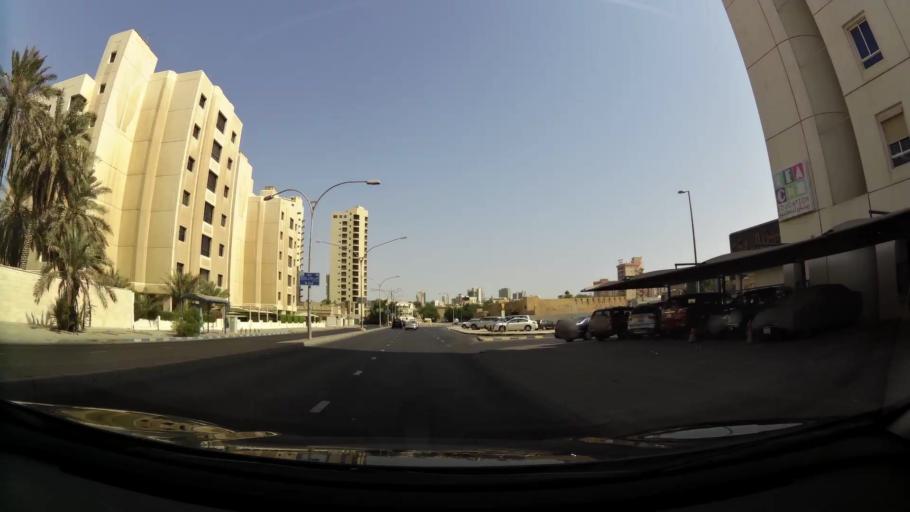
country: KW
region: Muhafazat Hawalli
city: As Salimiyah
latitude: 29.3378
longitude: 48.0610
